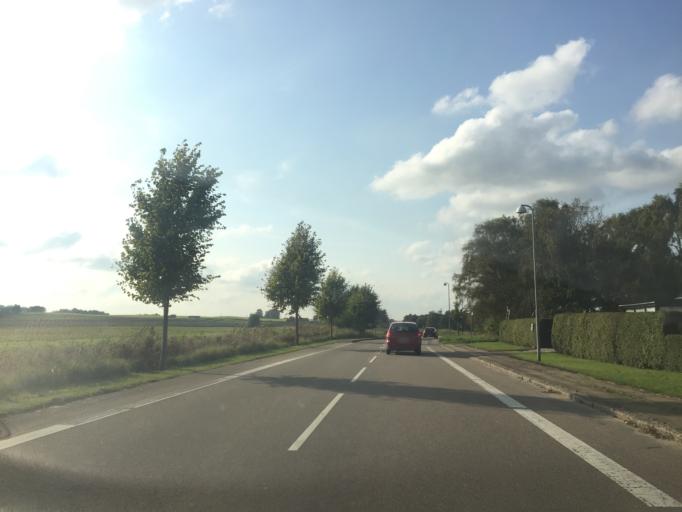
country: DK
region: Zealand
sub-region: Kalundborg Kommune
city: Svebolle
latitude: 55.6632
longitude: 11.2604
